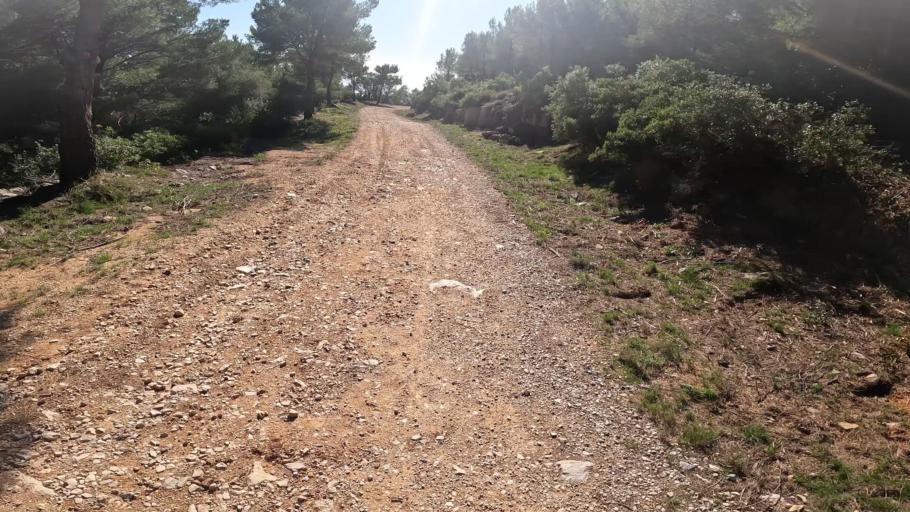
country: ES
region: Valencia
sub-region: Provincia de Castello
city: Alcoceber
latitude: 40.2717
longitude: 0.2769
